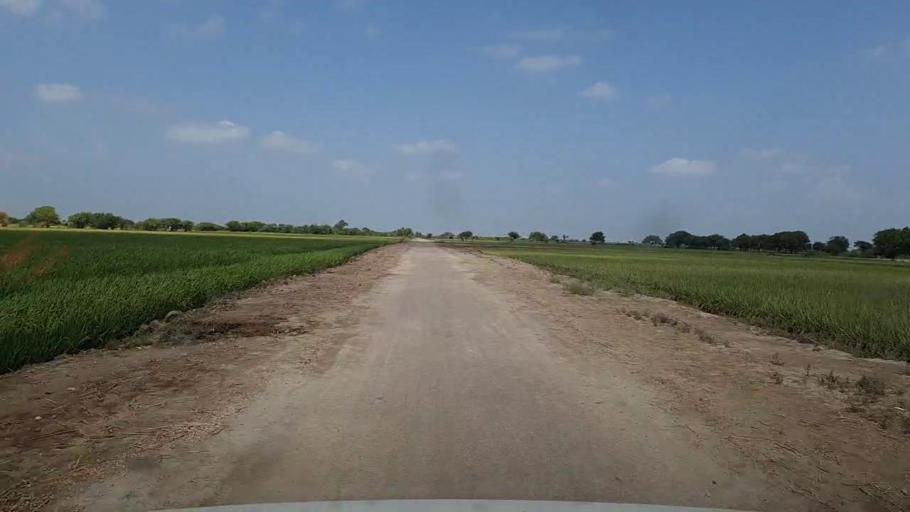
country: PK
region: Sindh
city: Kario
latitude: 24.6872
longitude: 68.5881
